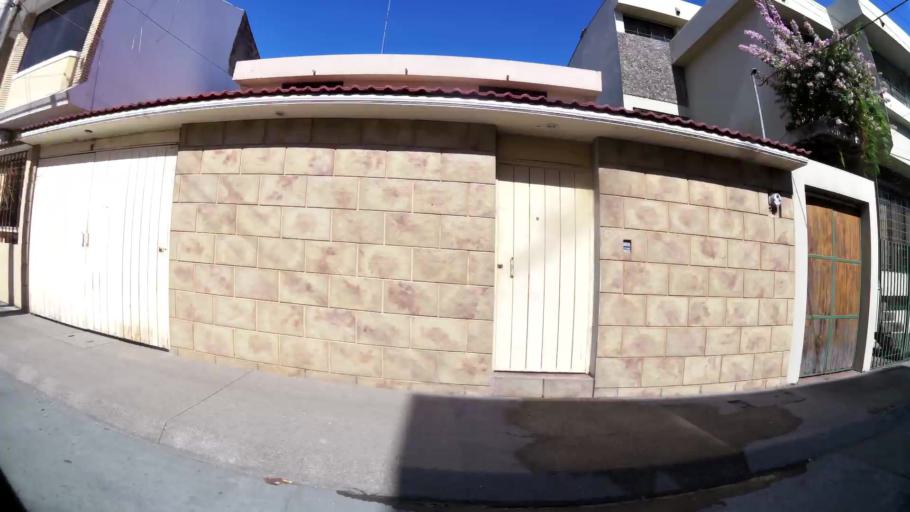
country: EC
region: Guayas
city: Eloy Alfaro
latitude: -2.1466
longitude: -79.9040
